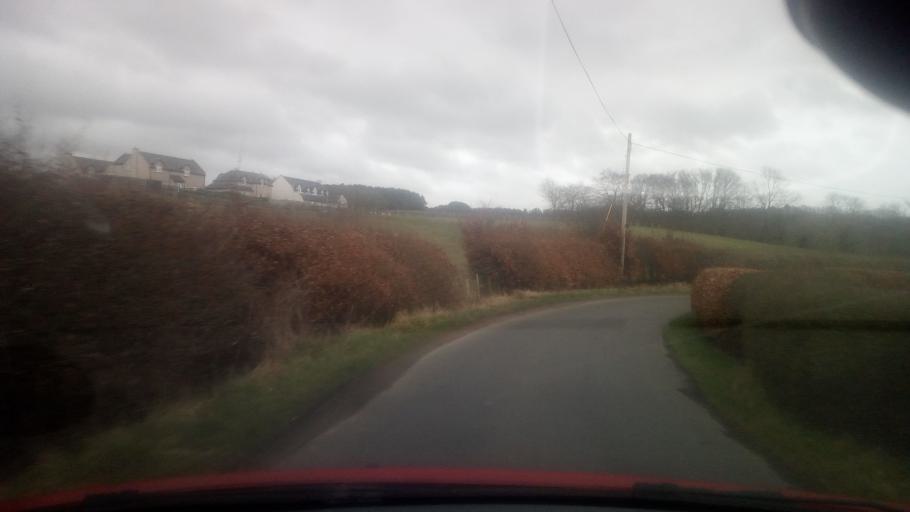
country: GB
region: Scotland
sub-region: The Scottish Borders
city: Jedburgh
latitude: 55.4758
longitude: -2.5406
